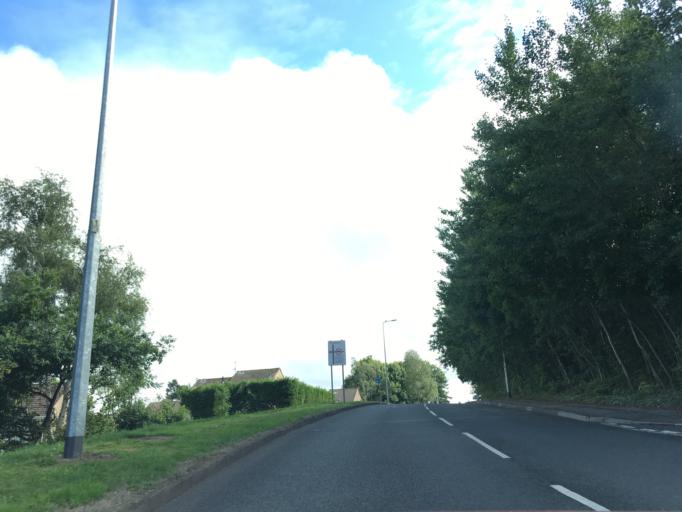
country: GB
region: Wales
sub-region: Cardiff
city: Cardiff
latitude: 51.5229
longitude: -3.1541
